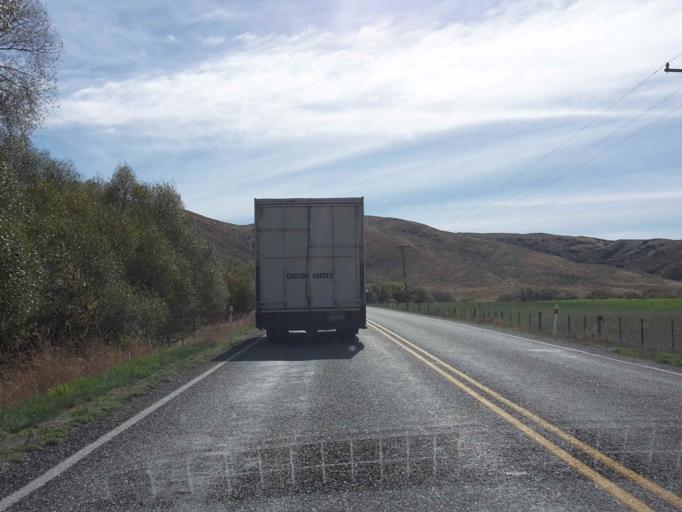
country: NZ
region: Otago
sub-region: Queenstown-Lakes District
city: Wanaka
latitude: -44.7061
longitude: 169.5028
